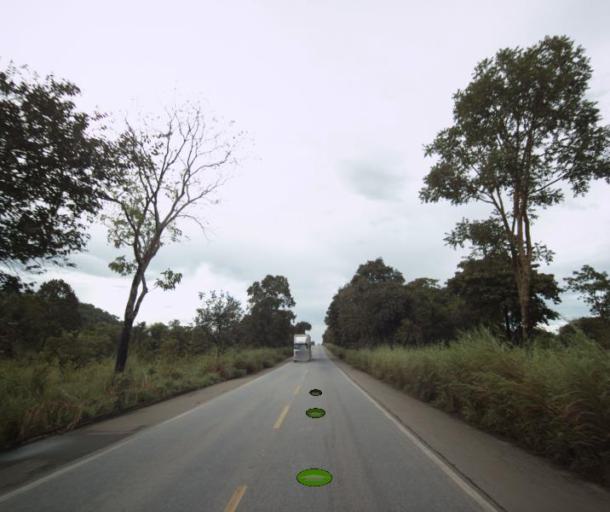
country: BR
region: Goias
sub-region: Porangatu
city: Porangatu
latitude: -13.6343
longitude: -49.0416
